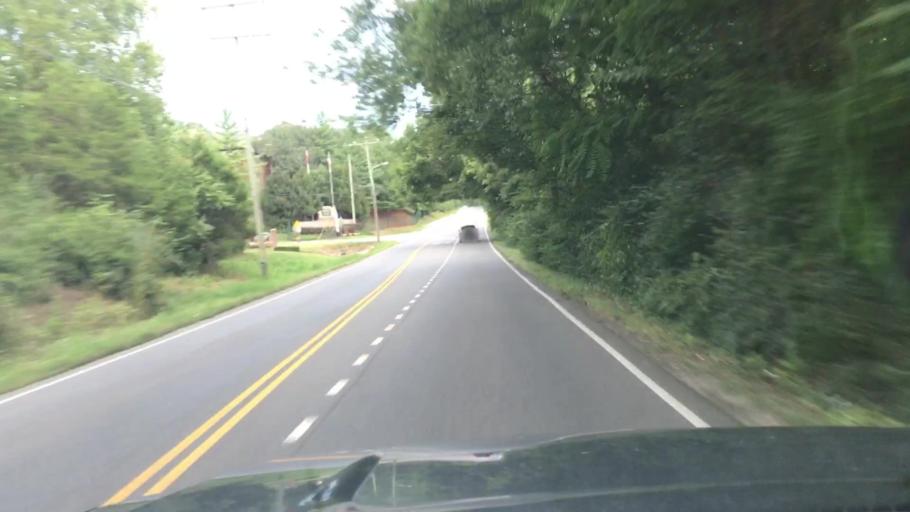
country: US
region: Tennessee
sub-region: Rutherford County
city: La Vergne
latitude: 36.0438
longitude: -86.6421
